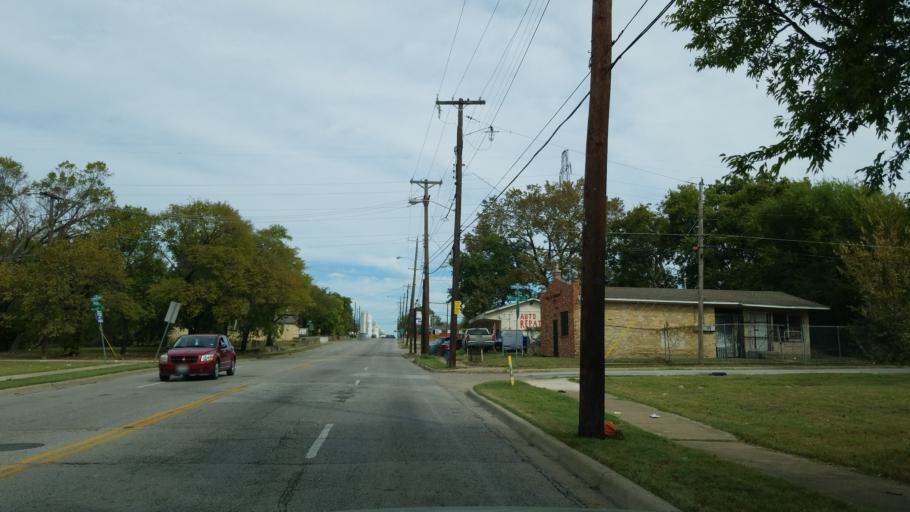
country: US
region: Texas
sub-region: Dallas County
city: Dallas
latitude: 32.7801
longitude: -96.7376
